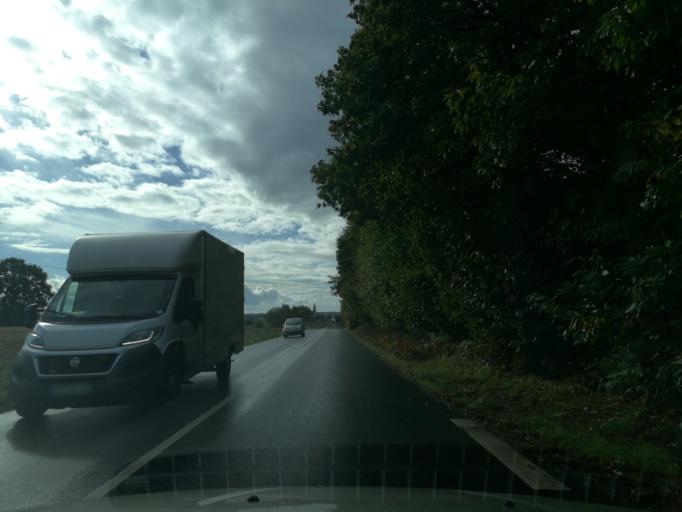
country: FR
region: Brittany
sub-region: Departement d'Ille-et-Vilaine
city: Bedee
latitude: 48.1967
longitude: -1.9403
